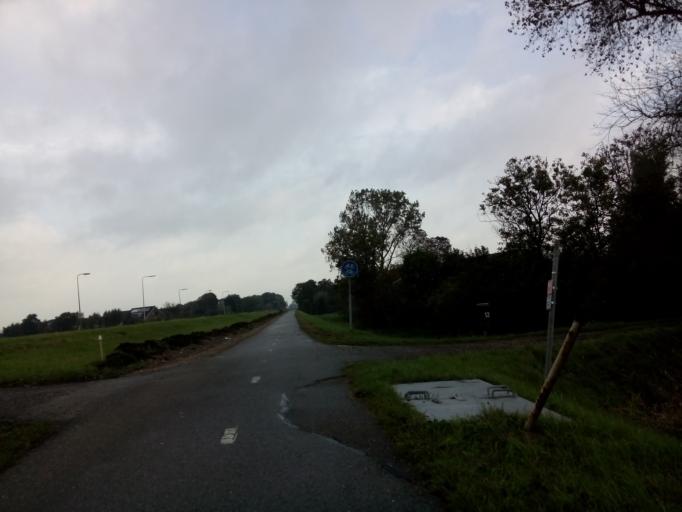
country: NL
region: South Holland
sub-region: Gemeente Westland
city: De Lier
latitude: 51.9617
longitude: 4.3017
